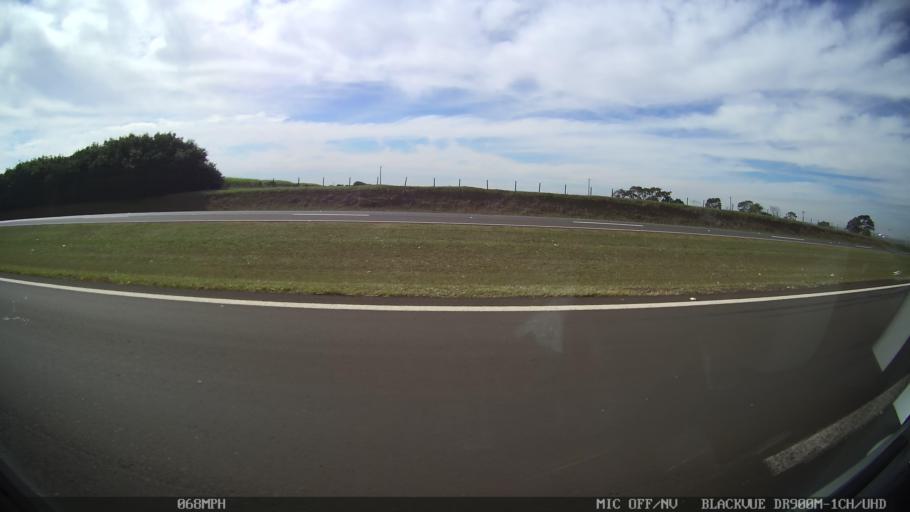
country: BR
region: Sao Paulo
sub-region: Matao
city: Matao
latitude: -21.6703
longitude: -48.3622
